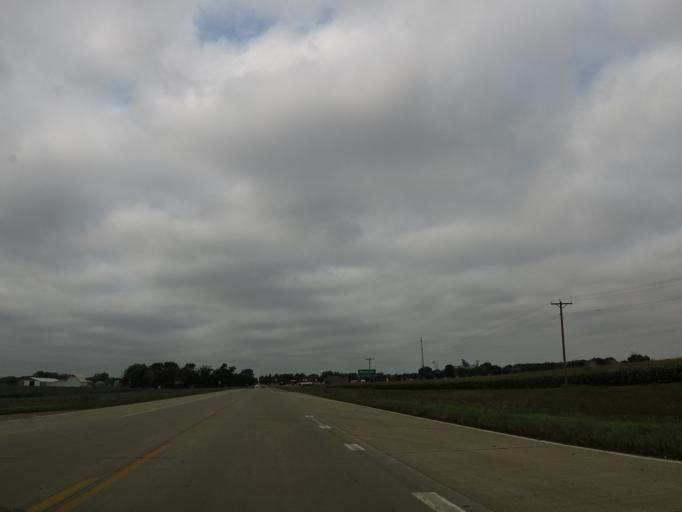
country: US
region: Minnesota
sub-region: Renville County
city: Renville
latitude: 44.7893
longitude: -95.1940
